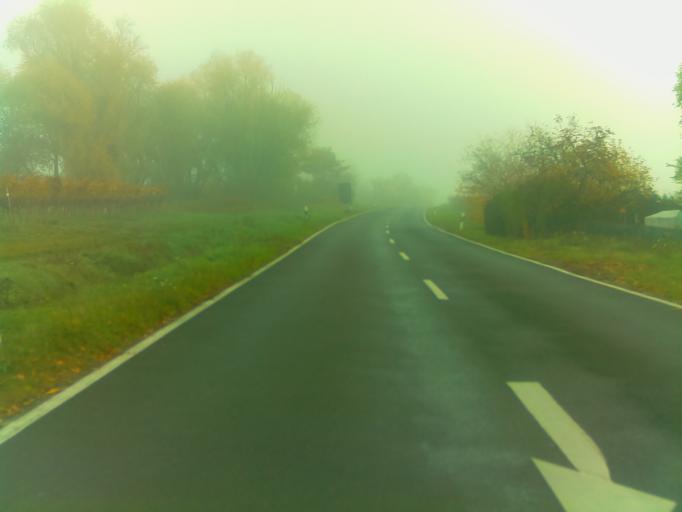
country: DE
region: Rheinland-Pfalz
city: Kallstadt
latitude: 49.4805
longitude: 8.1883
